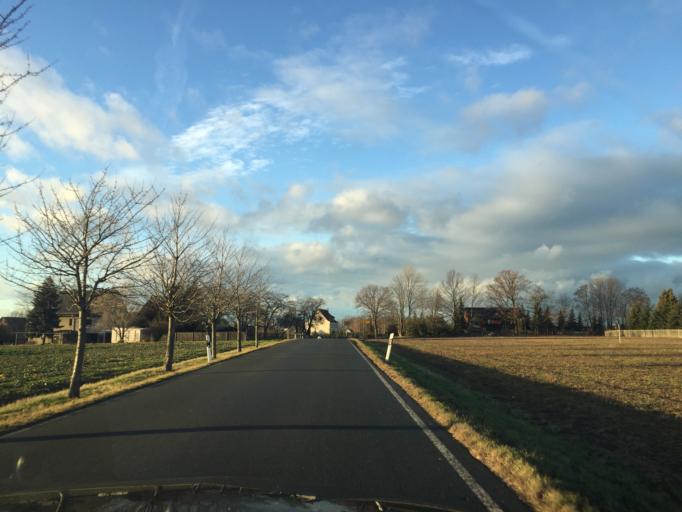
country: DE
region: Thuringia
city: Vollmershain
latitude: 50.8752
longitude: 12.3132
